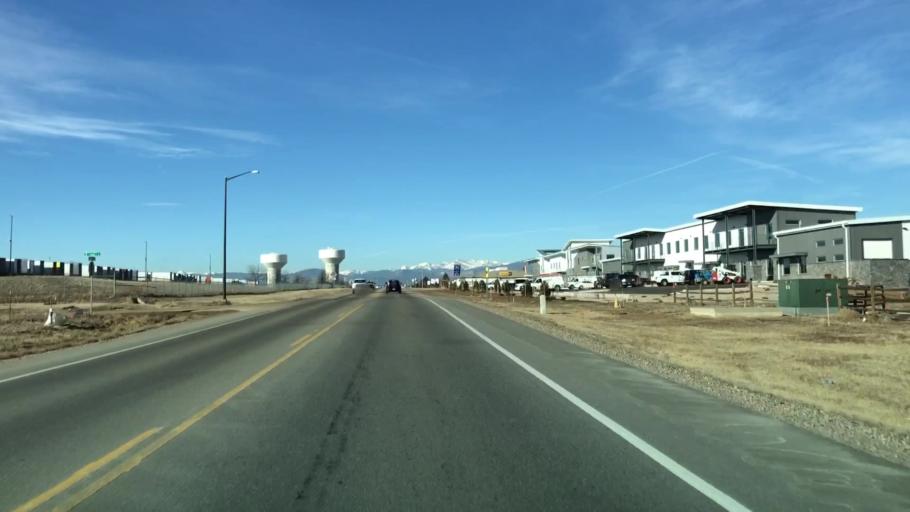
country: US
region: Colorado
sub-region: Weld County
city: Windsor
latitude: 40.4361
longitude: -104.9631
